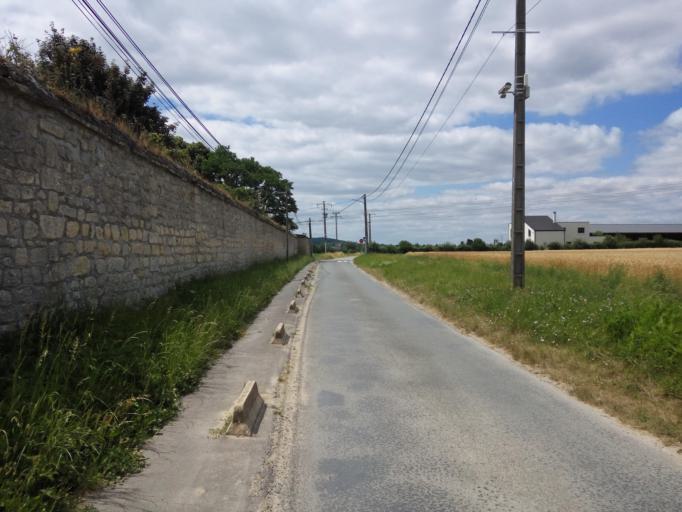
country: FR
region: Picardie
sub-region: Departement de l'Oise
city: Boran-sur-Oise
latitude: 49.1608
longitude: 2.3518
